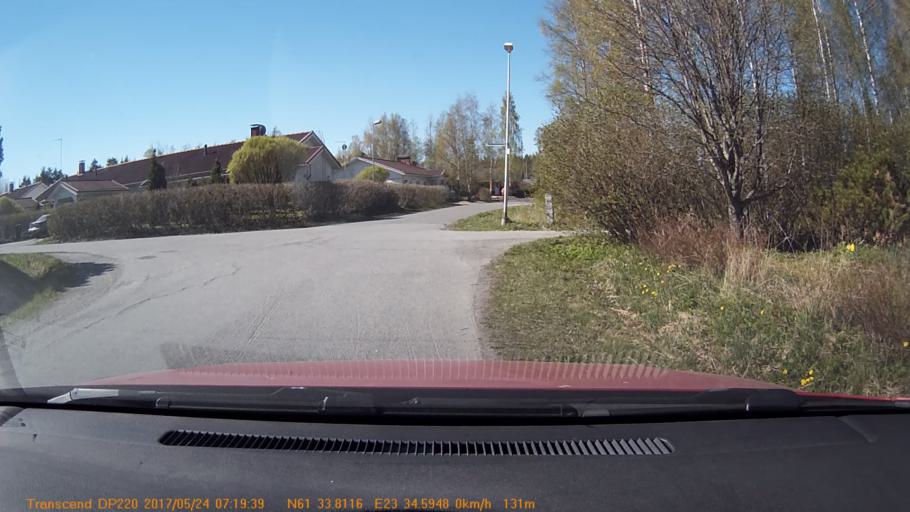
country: FI
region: Pirkanmaa
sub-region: Tampere
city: Yloejaervi
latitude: 61.5635
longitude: 23.5766
